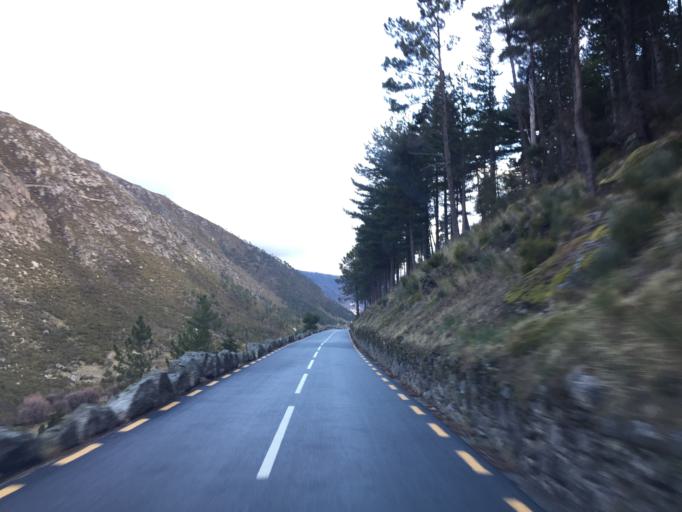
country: PT
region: Guarda
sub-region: Manteigas
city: Manteigas
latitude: 40.3514
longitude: -7.5598
